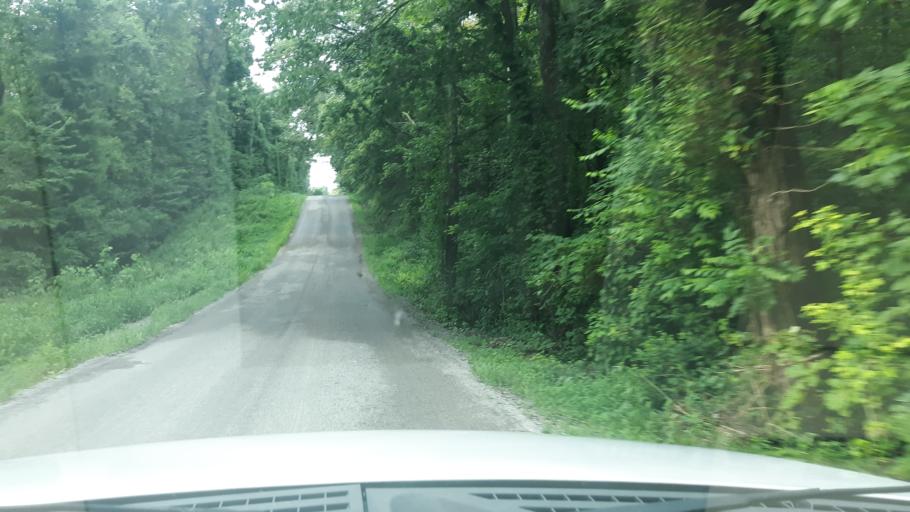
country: US
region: Illinois
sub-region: Saline County
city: Harrisburg
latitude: 37.8487
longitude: -88.5814
